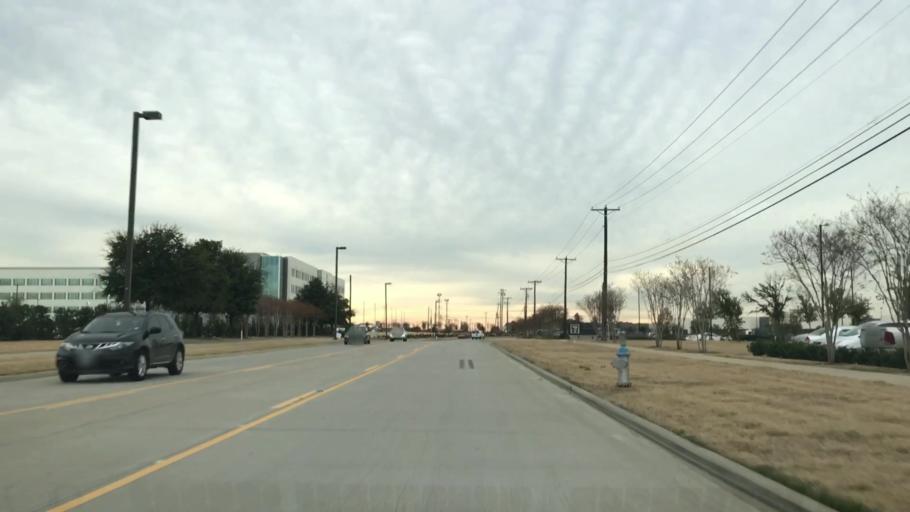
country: US
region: Texas
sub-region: Dallas County
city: Coppell
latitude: 32.9257
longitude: -96.9886
